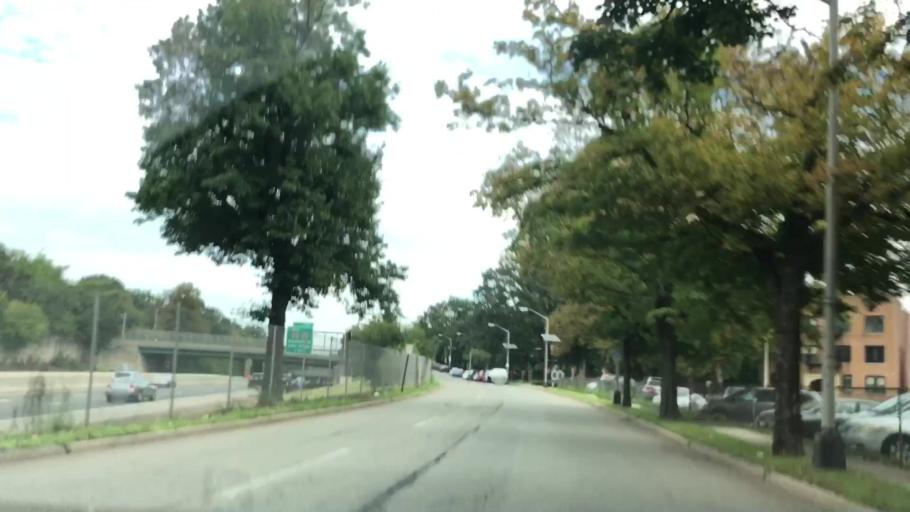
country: US
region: New Jersey
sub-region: Essex County
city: East Orange
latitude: 40.7678
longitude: -74.2040
